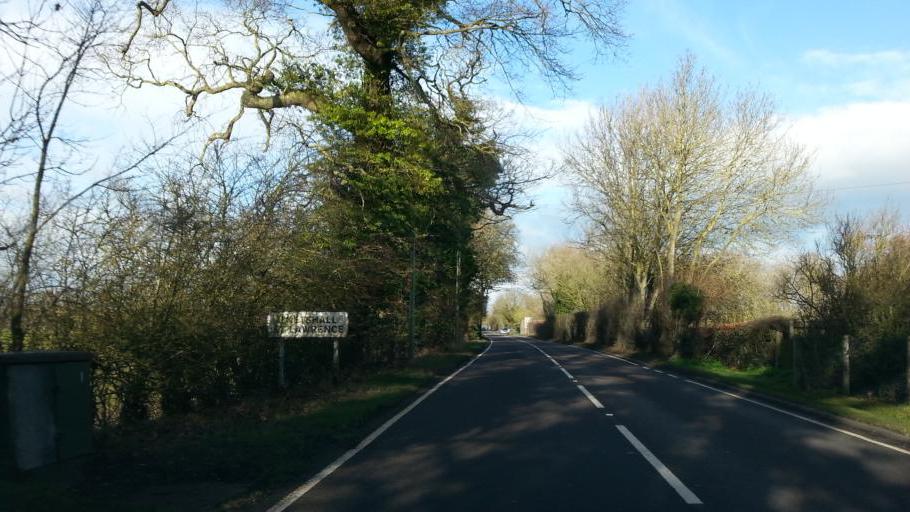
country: GB
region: England
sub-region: Suffolk
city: Halesworth
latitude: 52.3930
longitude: 1.4991
